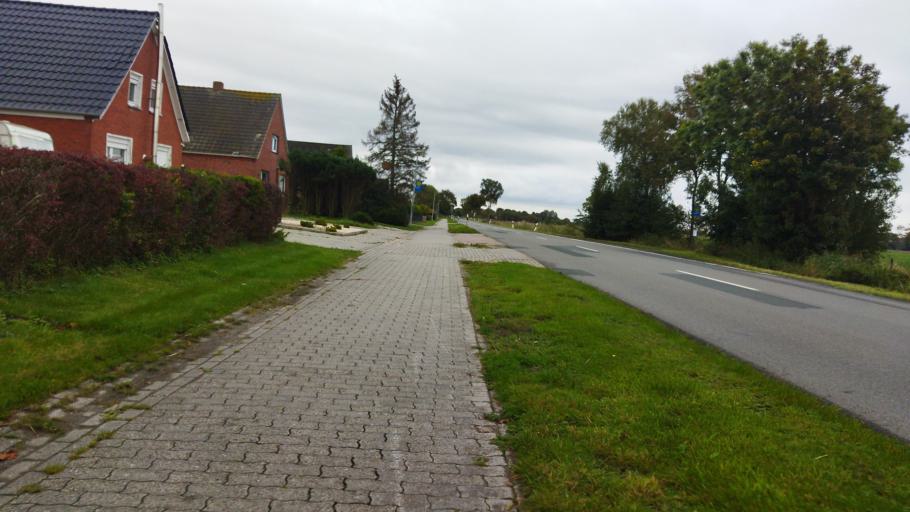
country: DE
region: Lower Saxony
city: Hinte
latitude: 53.4338
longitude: 7.1743
